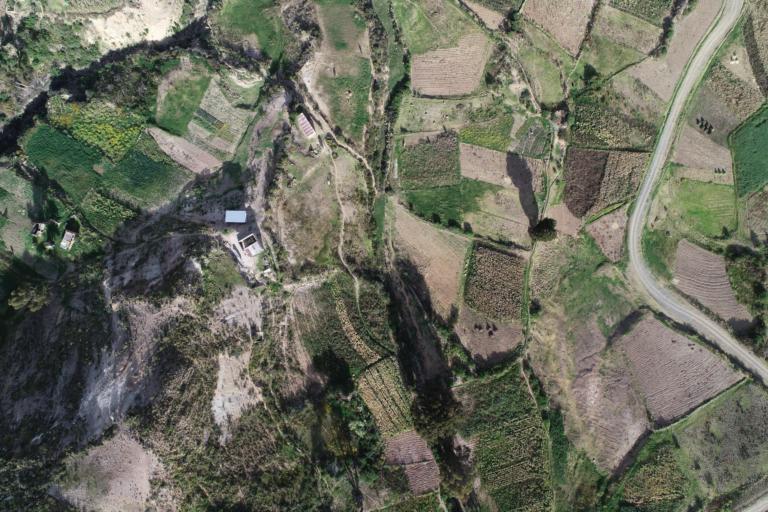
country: BO
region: La Paz
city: La Paz
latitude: -16.5526
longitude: -67.9891
